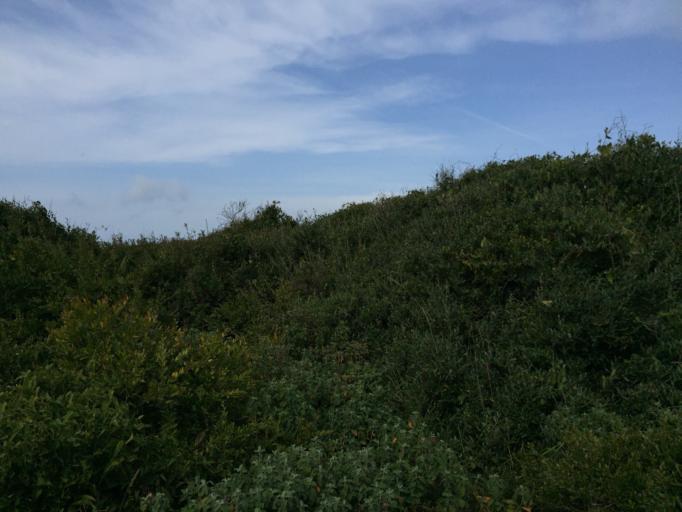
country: IT
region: Campania
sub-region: Provincia di Napoli
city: Monterusciello
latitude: 40.8489
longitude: 14.0479
